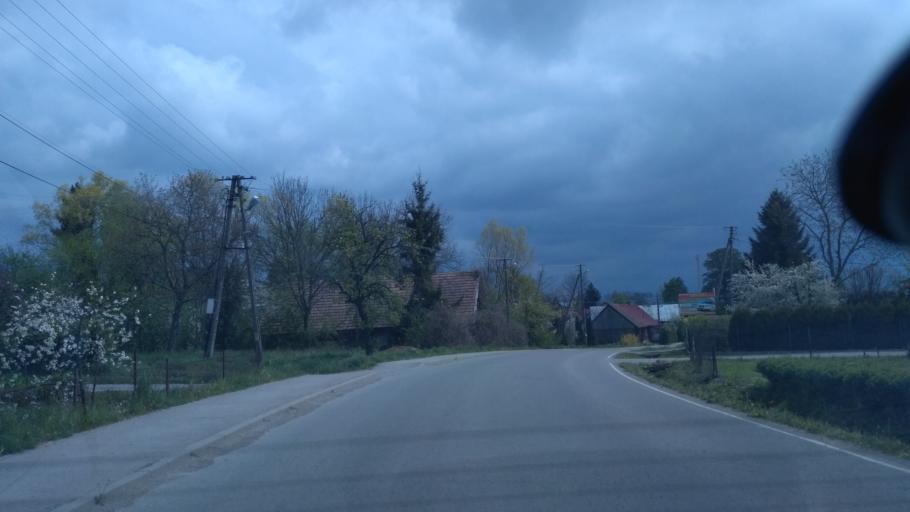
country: PL
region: Subcarpathian Voivodeship
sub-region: Powiat brzozowski
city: Haczow
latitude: 49.6456
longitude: 21.9298
